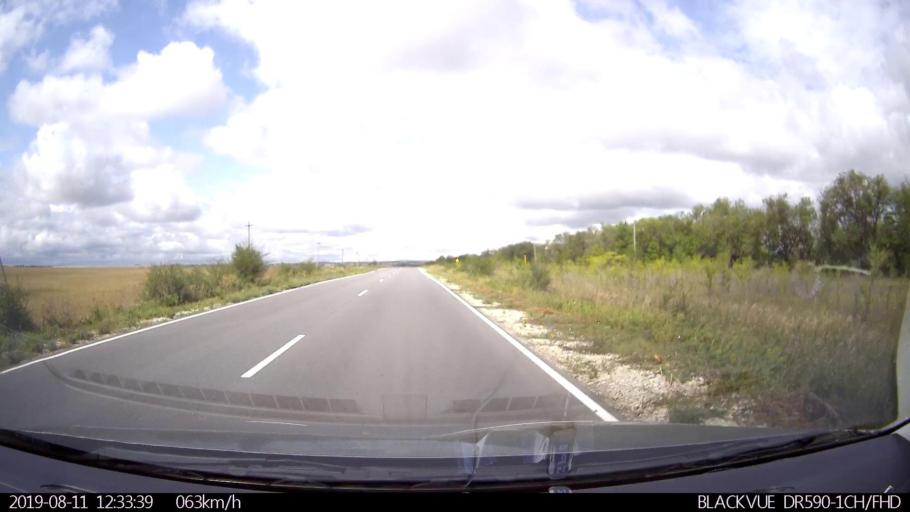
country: RU
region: Ulyanovsk
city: Ignatovka
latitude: 53.8110
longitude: 47.8532
